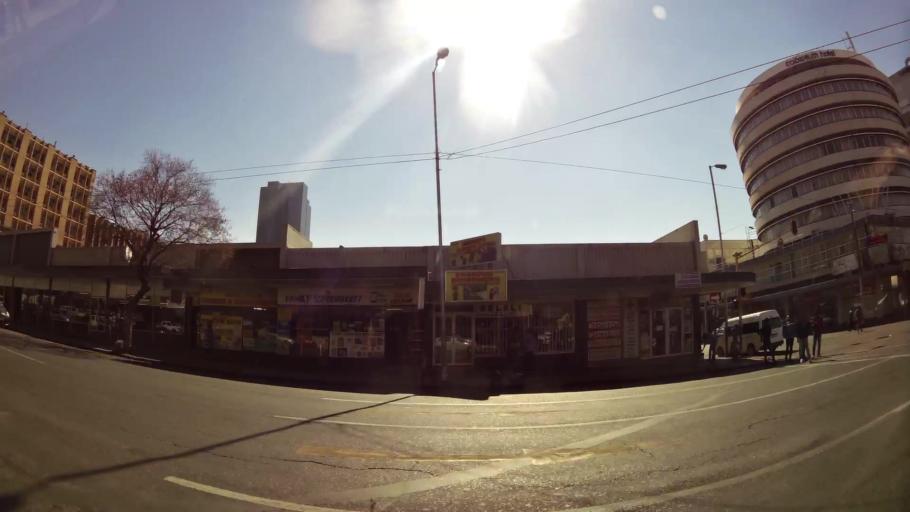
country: ZA
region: Gauteng
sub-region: City of Tshwane Metropolitan Municipality
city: Pretoria
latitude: -25.7487
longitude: 28.1979
